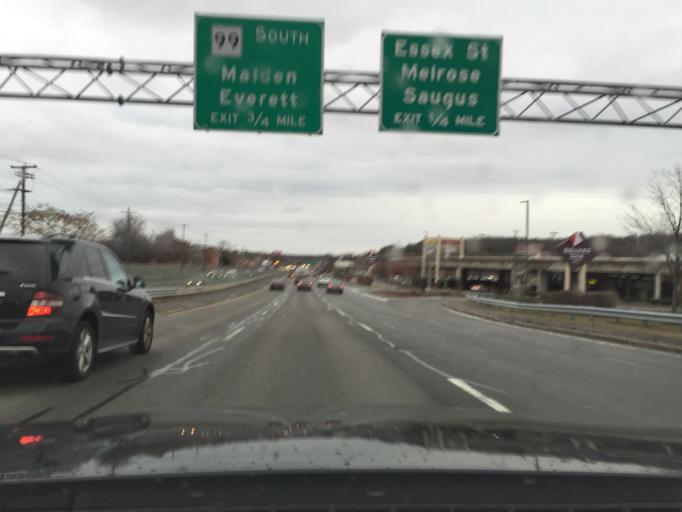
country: US
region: Massachusetts
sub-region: Essex County
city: Saugus
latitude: 42.4632
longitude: -71.0249
